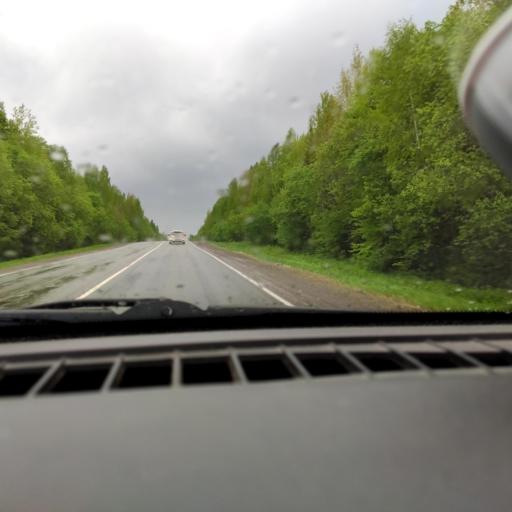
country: RU
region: Perm
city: Perm
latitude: 58.1725
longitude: 56.2331
